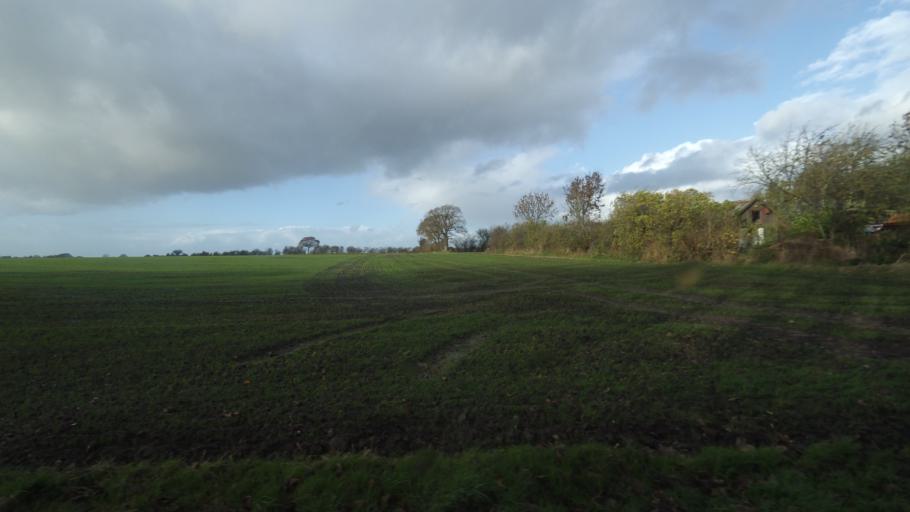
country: DK
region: Central Jutland
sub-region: Odder Kommune
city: Odder
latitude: 55.9018
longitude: 10.1950
